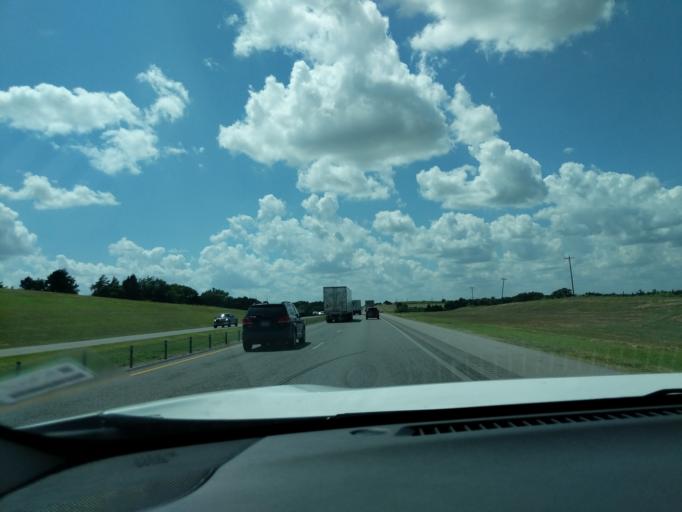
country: US
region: Oklahoma
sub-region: Caddo County
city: Hinton
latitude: 35.5251
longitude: -98.3148
